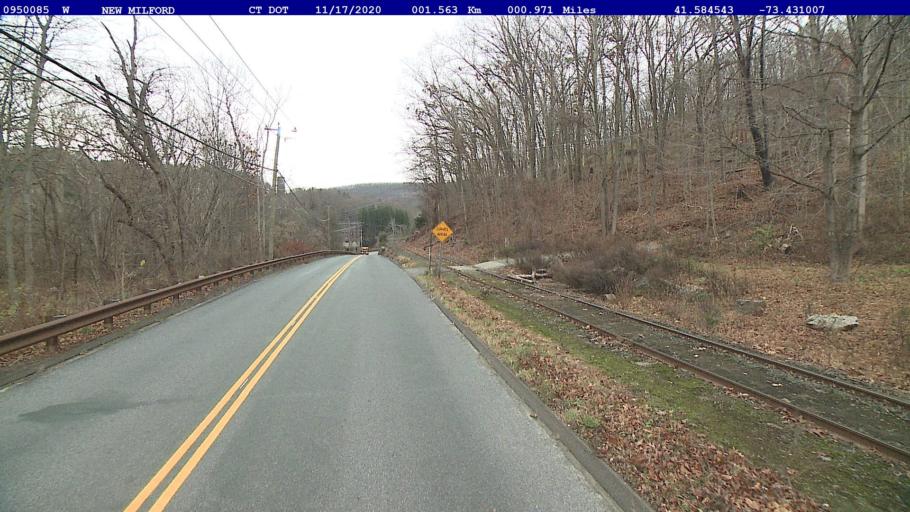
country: US
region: Connecticut
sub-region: Litchfield County
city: New Milford
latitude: 41.5845
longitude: -73.4311
